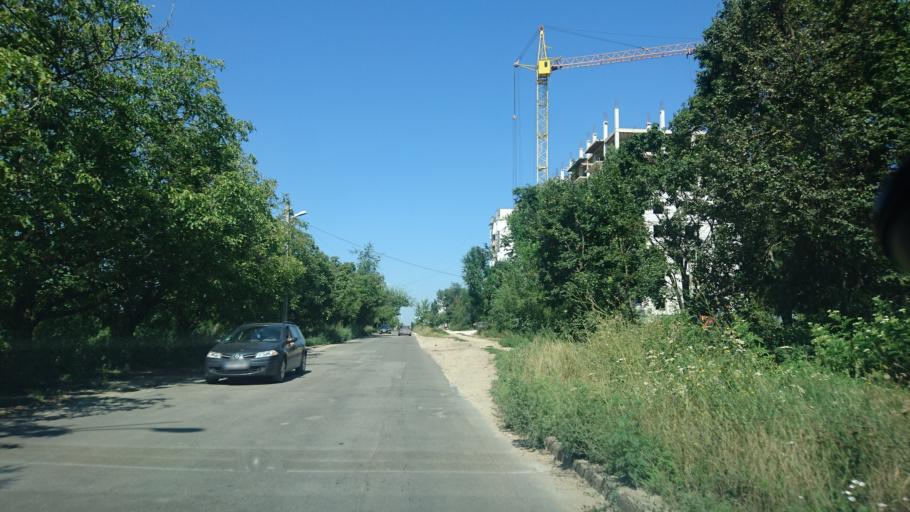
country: MD
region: Laloveni
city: Ialoveni
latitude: 47.0004
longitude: 28.7795
